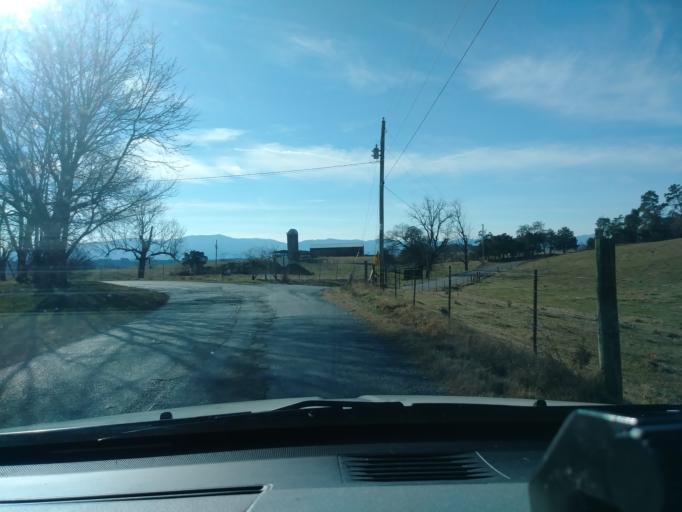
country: US
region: Tennessee
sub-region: Greene County
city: Greeneville
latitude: 36.0877
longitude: -82.9018
